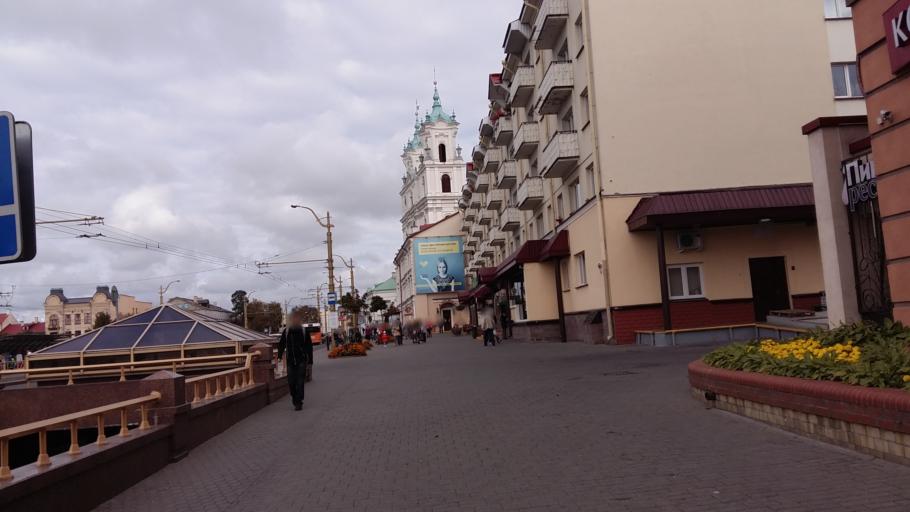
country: BY
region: Grodnenskaya
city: Hrodna
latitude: 53.6769
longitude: 23.8302
